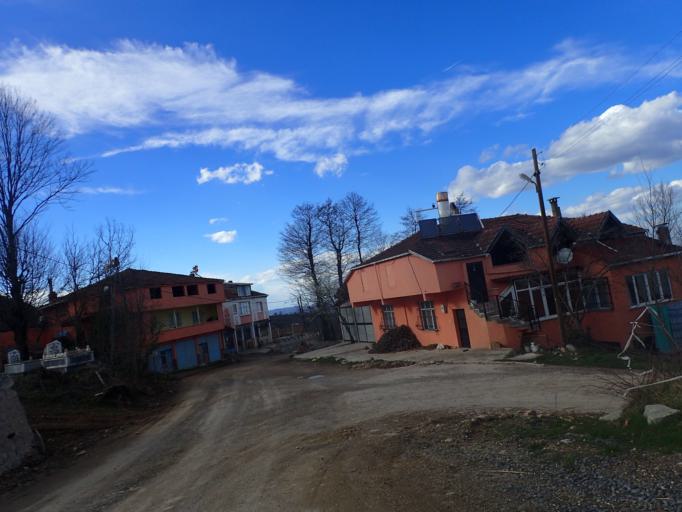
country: TR
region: Ordu
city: Kumru
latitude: 40.9281
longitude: 37.2472
